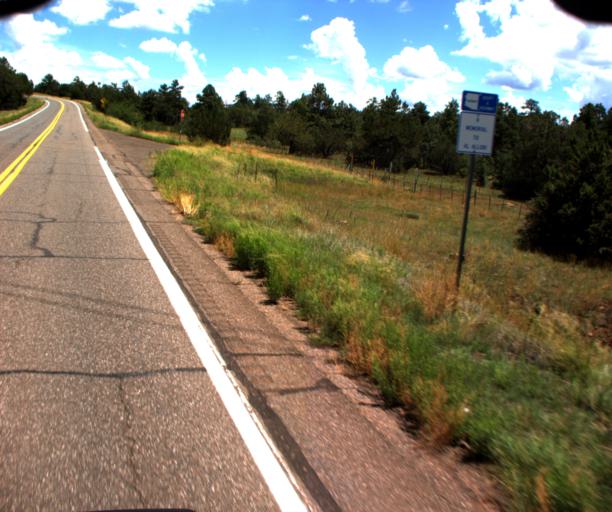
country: US
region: Arizona
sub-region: Gila County
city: Pine
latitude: 34.5111
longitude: -111.5461
